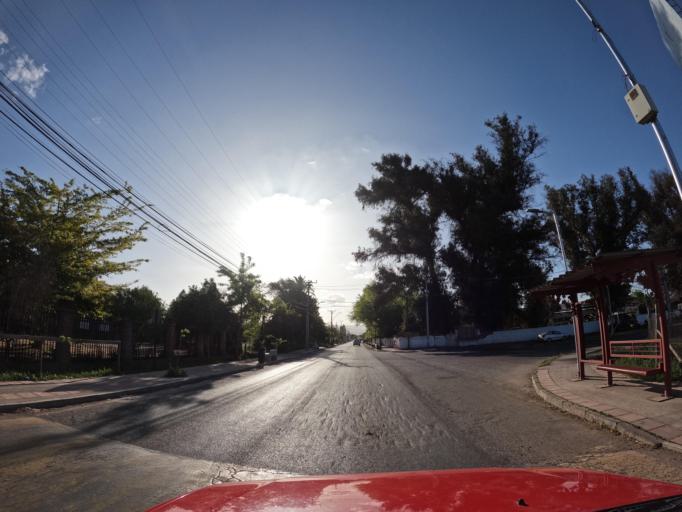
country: CL
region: O'Higgins
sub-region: Provincia de Colchagua
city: Santa Cruz
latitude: -34.6492
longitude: -71.3550
